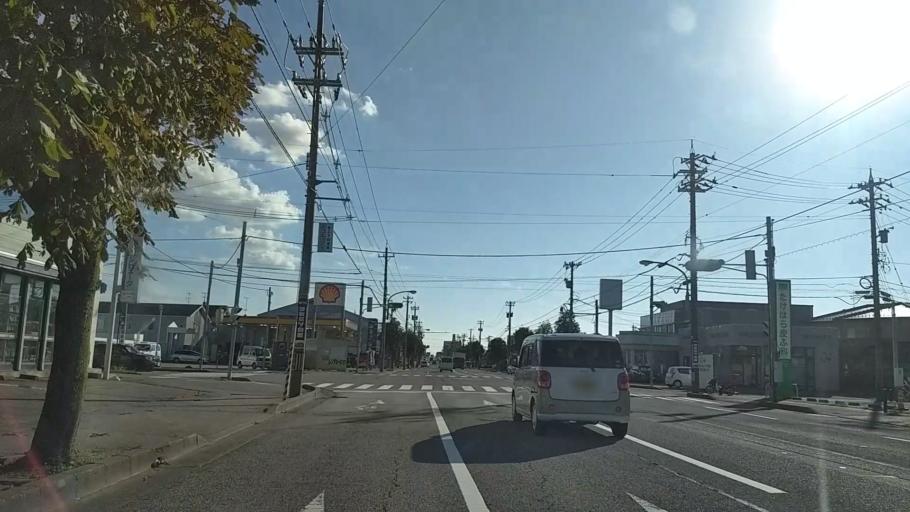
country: JP
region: Ishikawa
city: Kanazawa-shi
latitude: 36.5757
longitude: 136.6331
